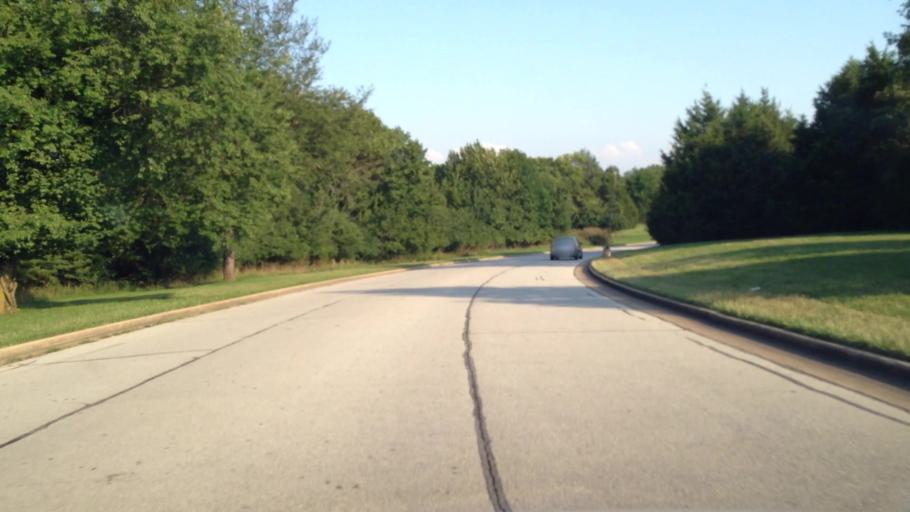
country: US
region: Missouri
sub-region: Jasper County
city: Duquesne
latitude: 37.0530
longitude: -94.4741
